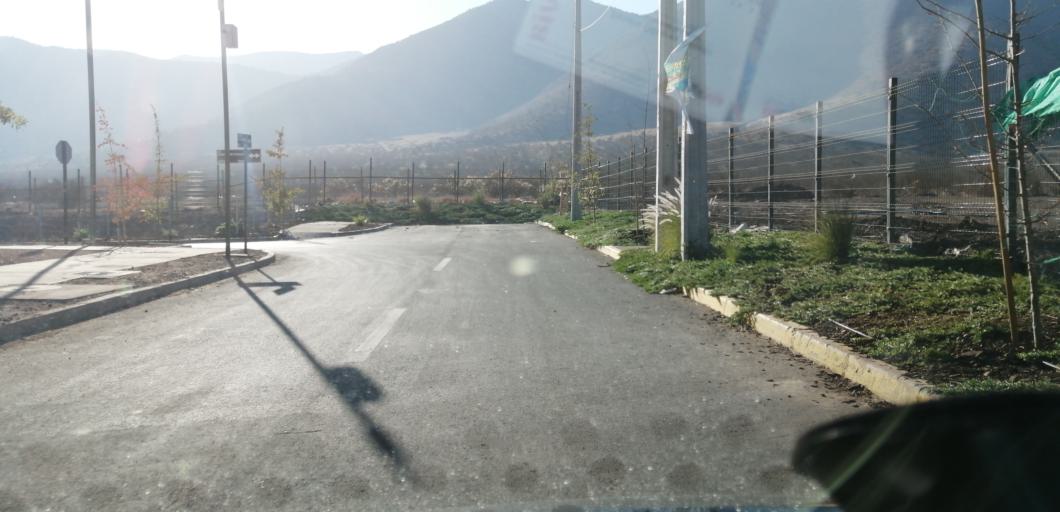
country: CL
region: Santiago Metropolitan
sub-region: Provincia de Santiago
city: Lo Prado
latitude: -33.4697
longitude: -70.8600
